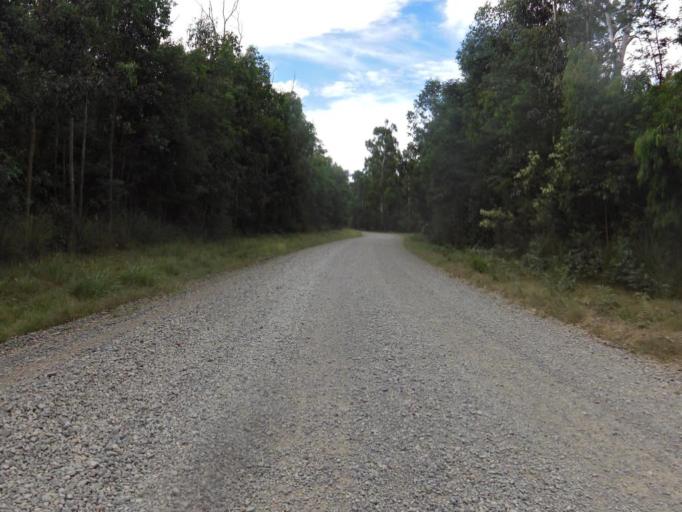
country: AU
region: Victoria
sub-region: Murrindindi
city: Alexandra
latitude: -37.3988
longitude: 145.5590
